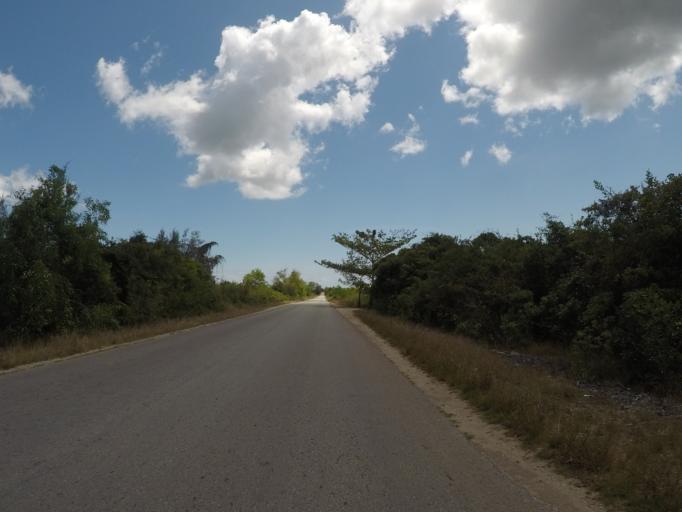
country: TZ
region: Zanzibar Central/South
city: Nganane
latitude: -6.2785
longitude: 39.4802
